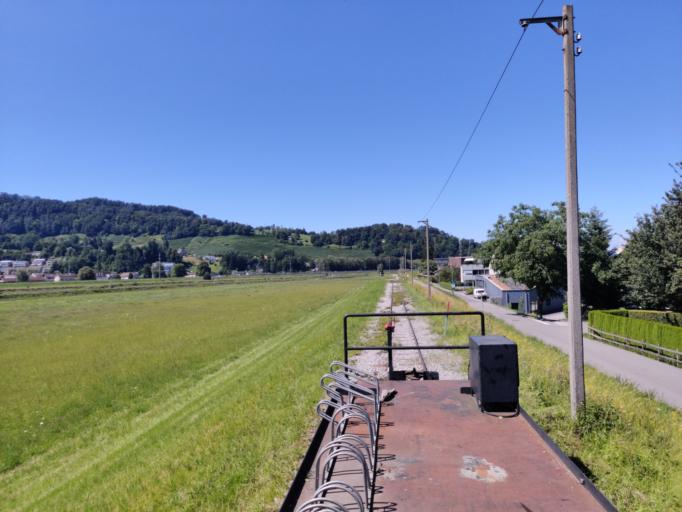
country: AT
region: Vorarlberg
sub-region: Politischer Bezirk Dornbirn
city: Lustenau
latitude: 47.4325
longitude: 9.6473
